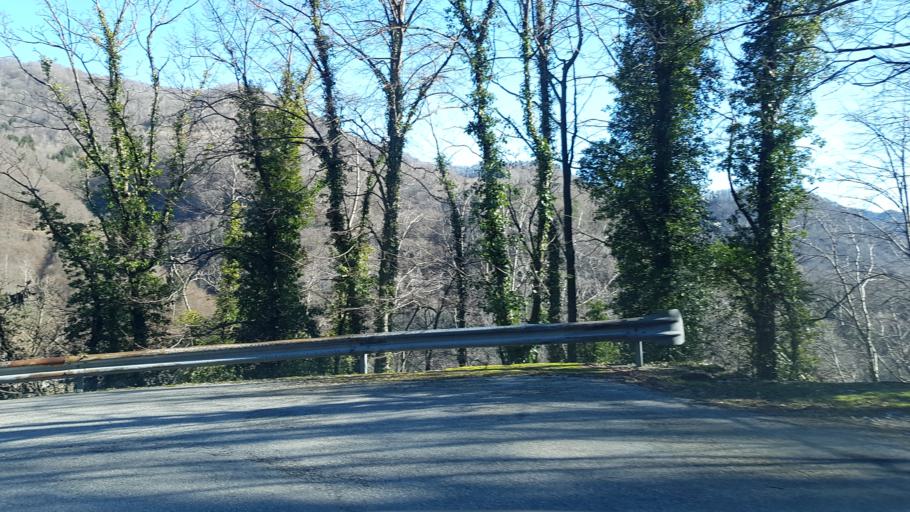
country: IT
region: Friuli Venezia Giulia
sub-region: Provincia di Udine
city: Taipana
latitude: 46.2324
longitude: 13.3030
